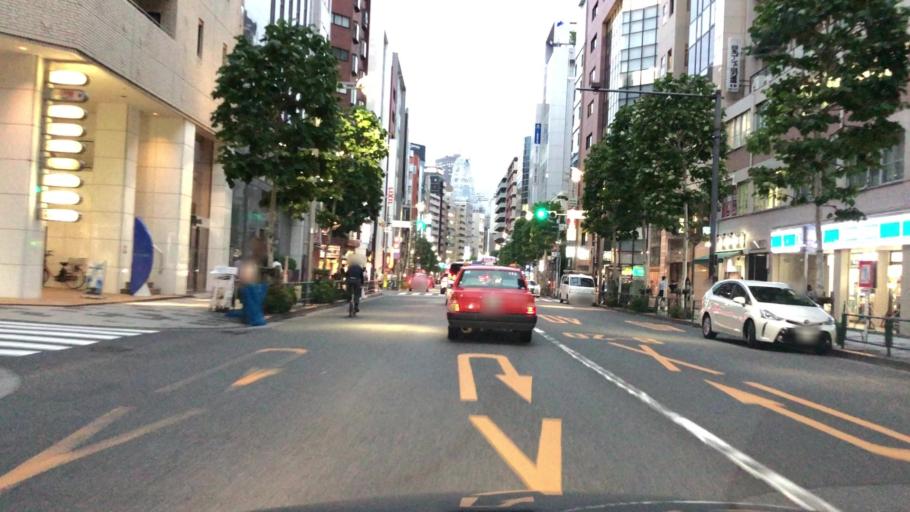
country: JP
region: Tokyo
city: Tokyo
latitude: 35.6882
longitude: 139.7124
